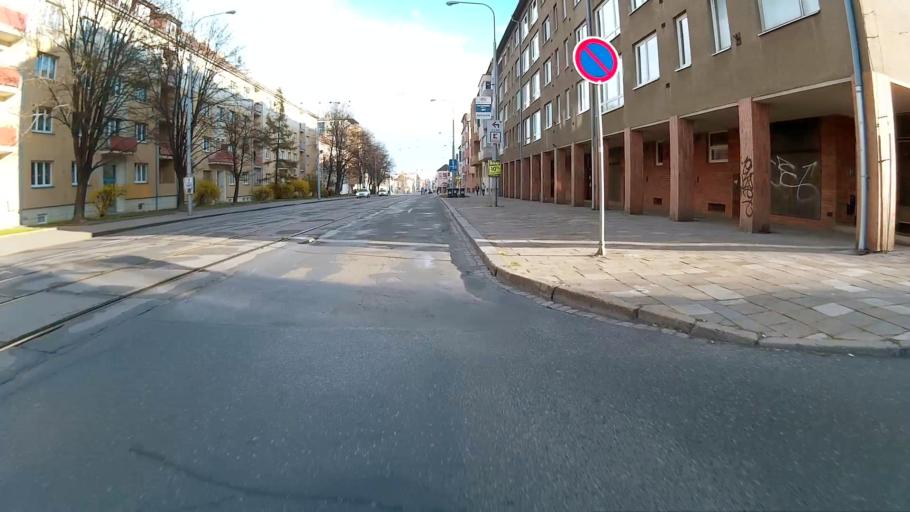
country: CZ
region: South Moravian
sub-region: Mesto Brno
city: Mokra Hora
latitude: 49.2293
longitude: 16.5914
